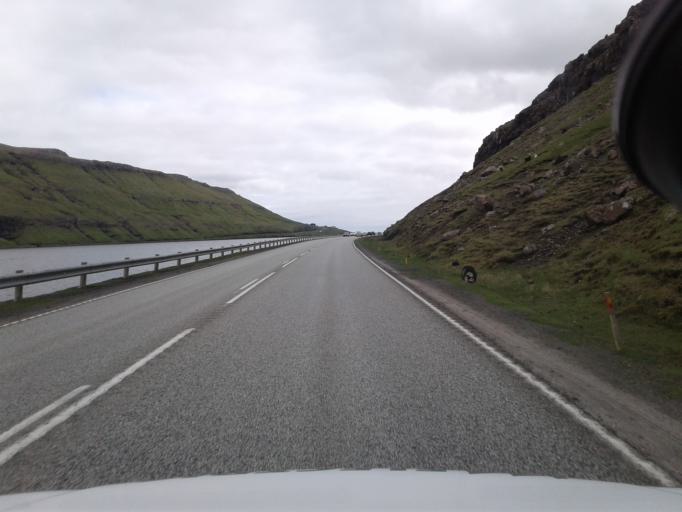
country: FO
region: Streymoy
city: Kollafjordhur
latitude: 62.0563
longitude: -6.8848
